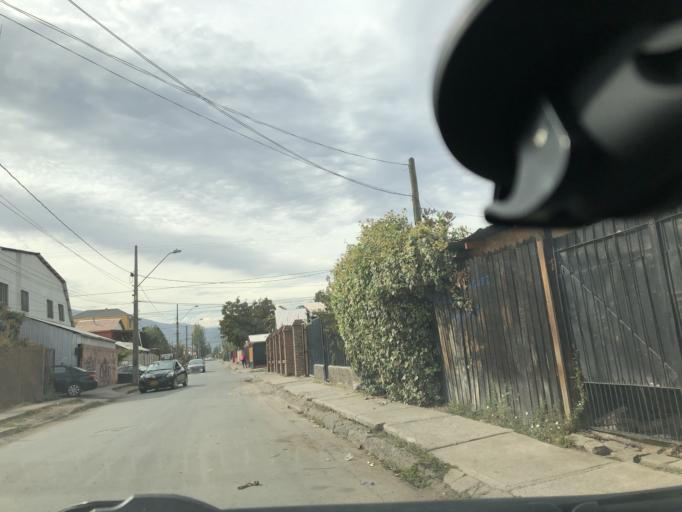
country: CL
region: Santiago Metropolitan
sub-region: Provincia de Cordillera
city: Puente Alto
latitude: -33.6121
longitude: -70.5222
